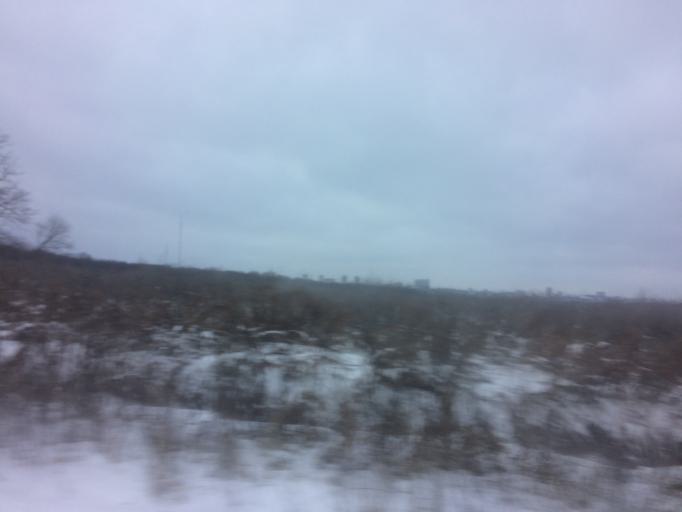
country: RU
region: Tula
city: Mendeleyevskiy
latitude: 54.1399
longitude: 37.6366
